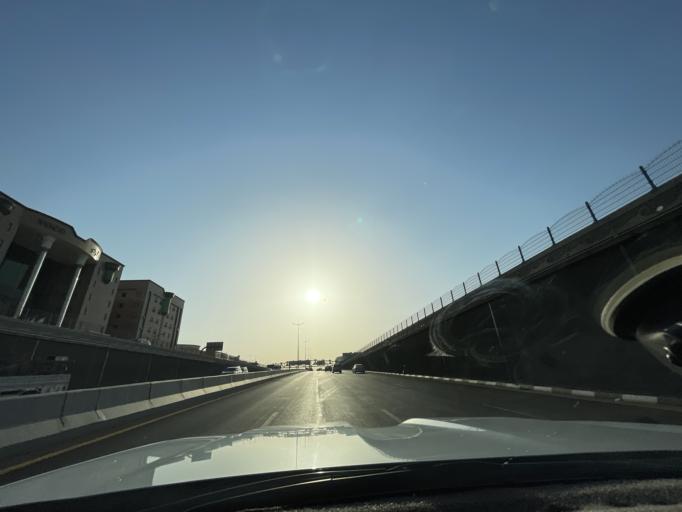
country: SA
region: Eastern Province
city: Khobar
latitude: 26.2869
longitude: 50.1876
